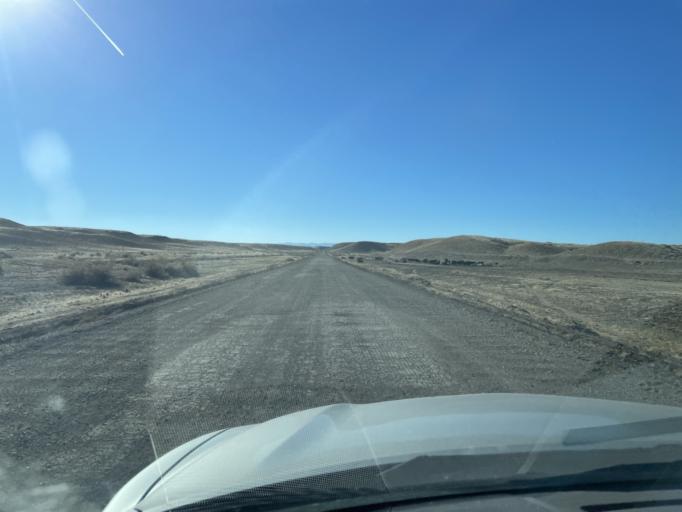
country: US
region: Colorado
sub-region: Mesa County
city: Loma
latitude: 39.2060
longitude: -109.0813
